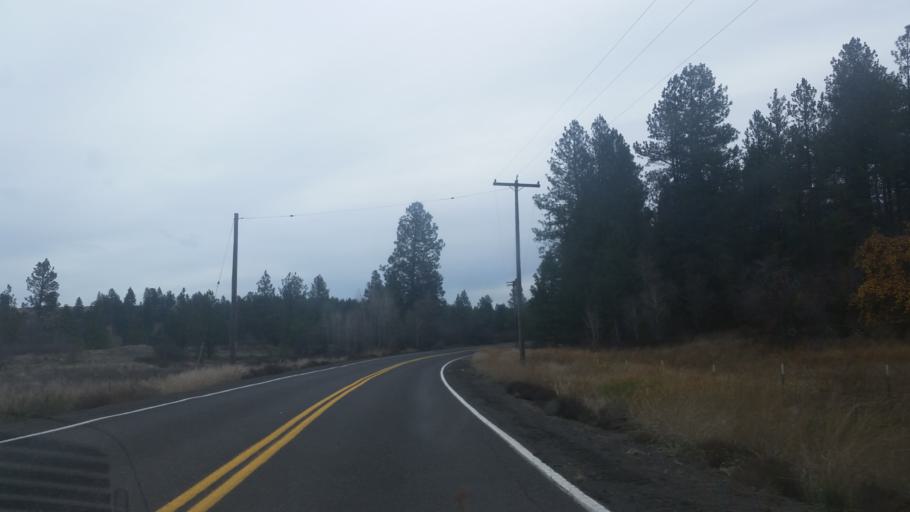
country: US
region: Washington
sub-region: Spokane County
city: Cheney
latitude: 47.2298
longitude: -117.4601
